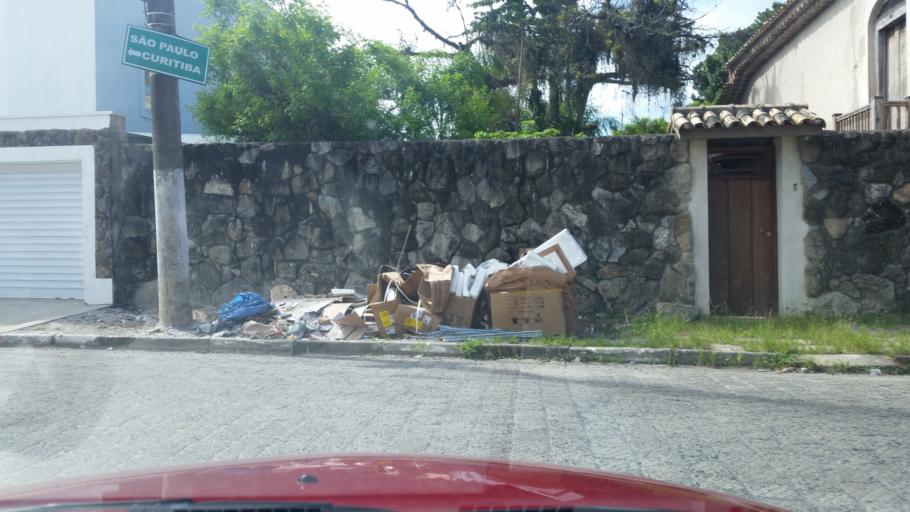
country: BR
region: Sao Paulo
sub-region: Iguape
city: Iguape
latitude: -24.7041
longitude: -47.5553
